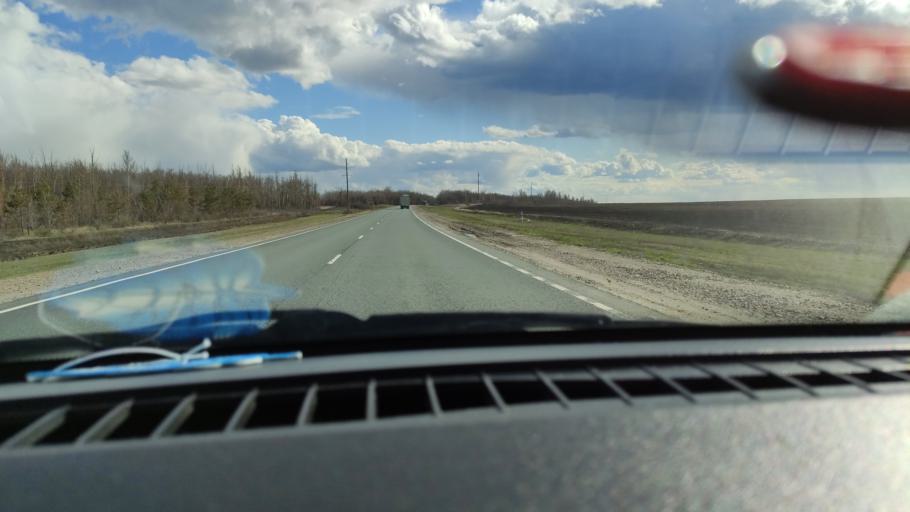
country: RU
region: Saratov
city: Alekseyevka
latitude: 52.2745
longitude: 47.9310
